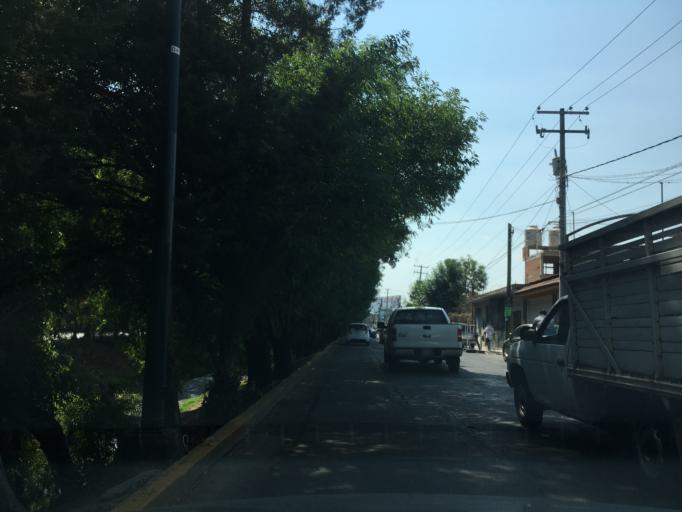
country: MX
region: Michoacan
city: Morelia
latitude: 19.6917
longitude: -101.1940
